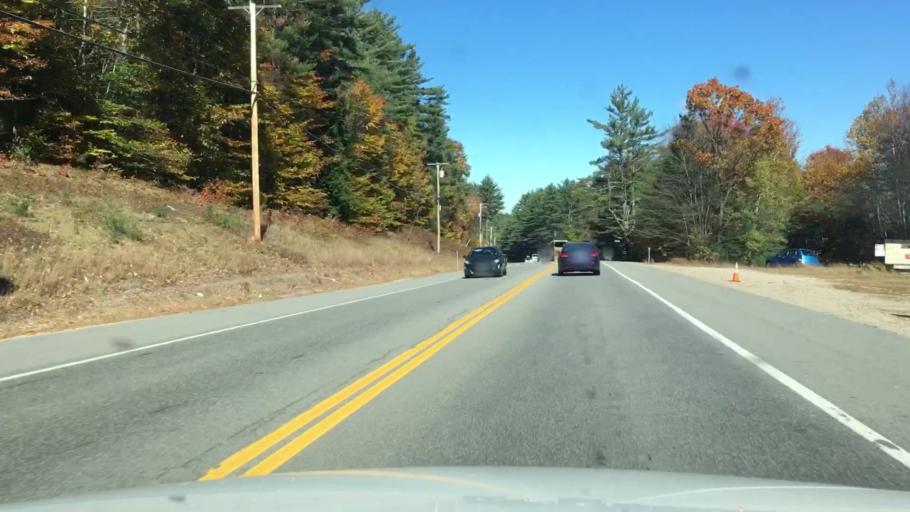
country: US
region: New Hampshire
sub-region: Carroll County
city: Ossipee
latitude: 43.7158
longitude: -71.1236
